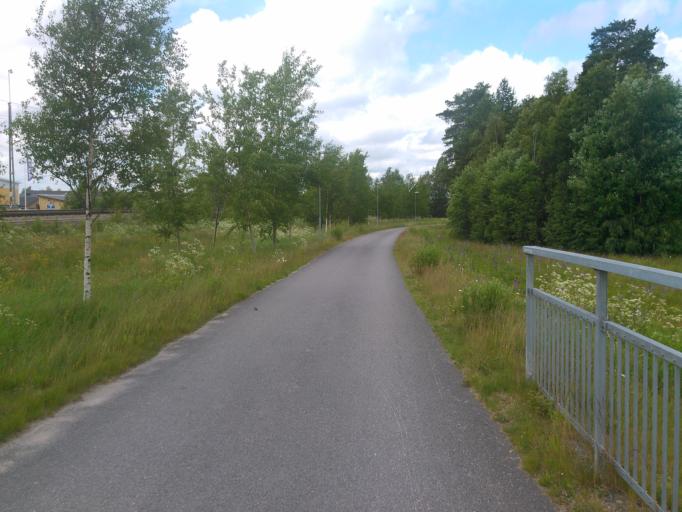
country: SE
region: Vaesterbotten
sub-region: Umea Kommun
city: Umea
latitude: 63.8383
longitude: 20.2479
